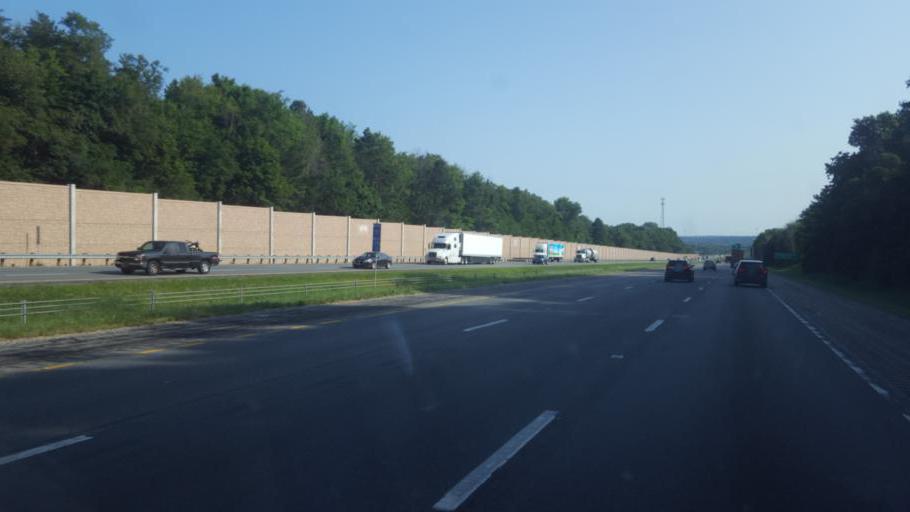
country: US
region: Ohio
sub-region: Richland County
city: Lincoln Heights
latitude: 40.7710
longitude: -82.4209
